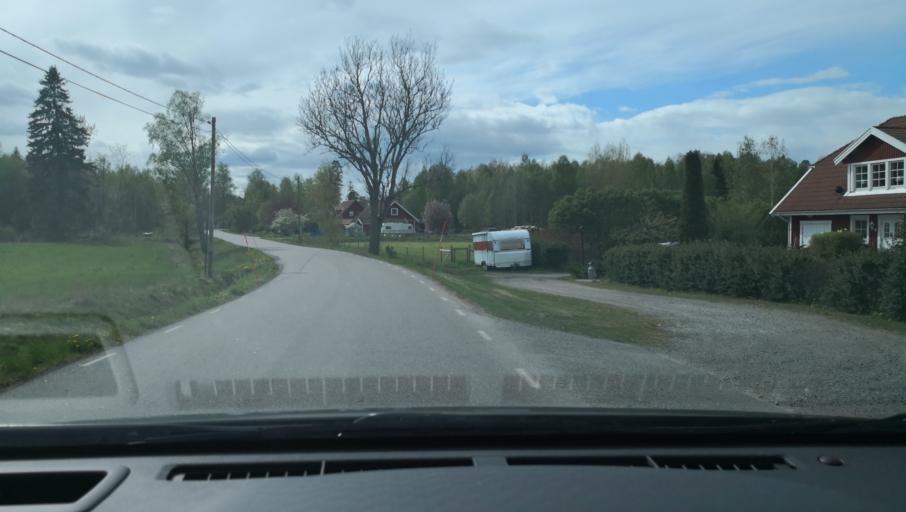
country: SE
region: OErebro
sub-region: Kumla Kommun
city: Hallabrottet
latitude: 59.1627
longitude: 15.2438
